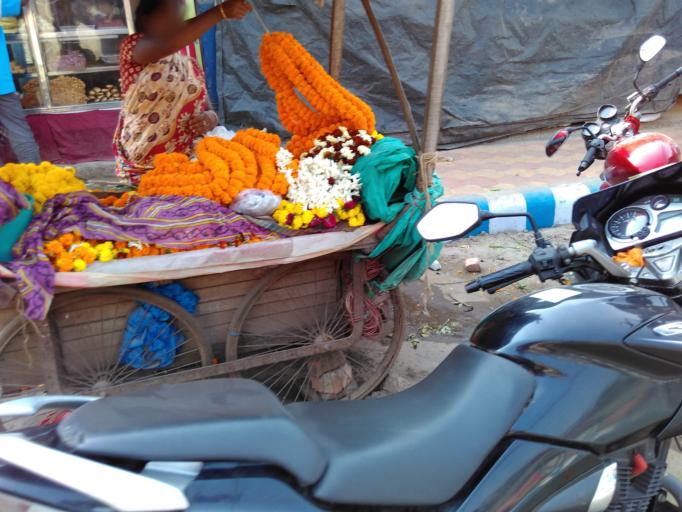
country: IN
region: West Bengal
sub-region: Kolkata
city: Kolkata
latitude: 22.4648
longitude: 88.3787
